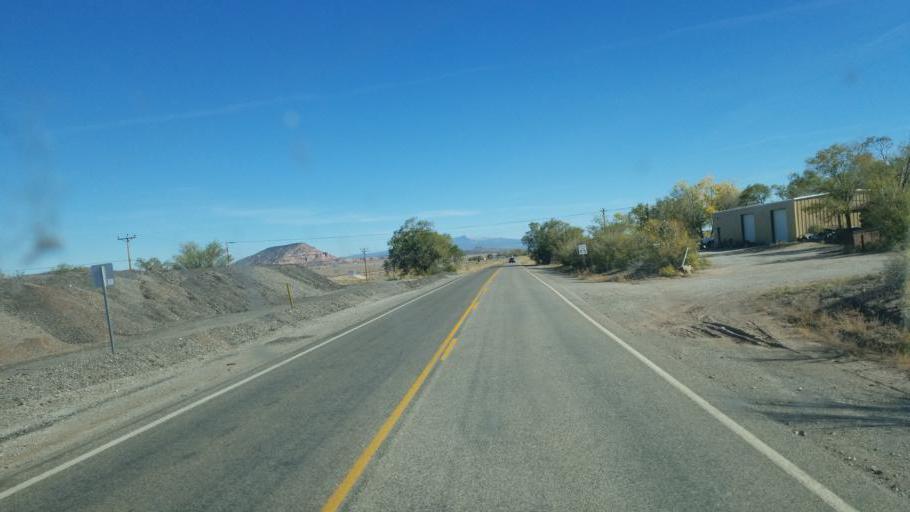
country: US
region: New Mexico
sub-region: McKinley County
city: Thoreau
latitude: 35.3644
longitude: -108.0435
